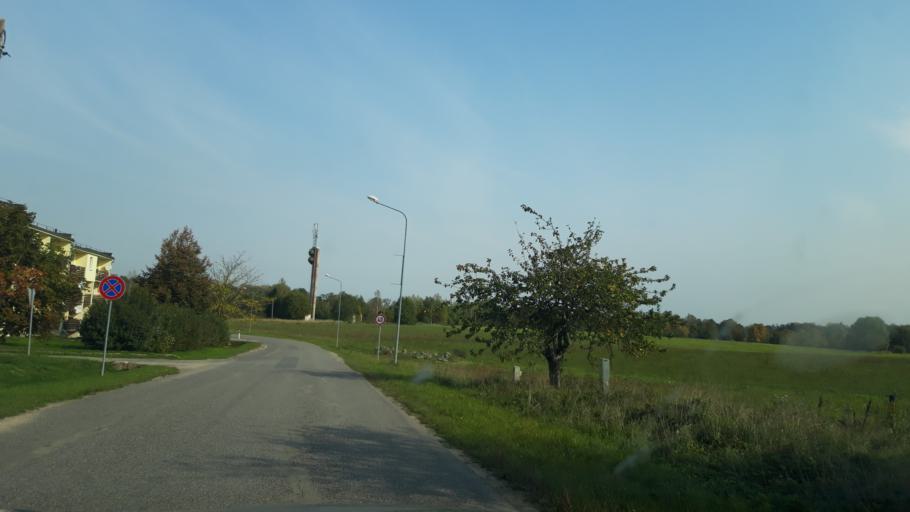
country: LV
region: Mazsalaca
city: Mazsalaca
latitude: 57.8558
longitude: 25.0433
